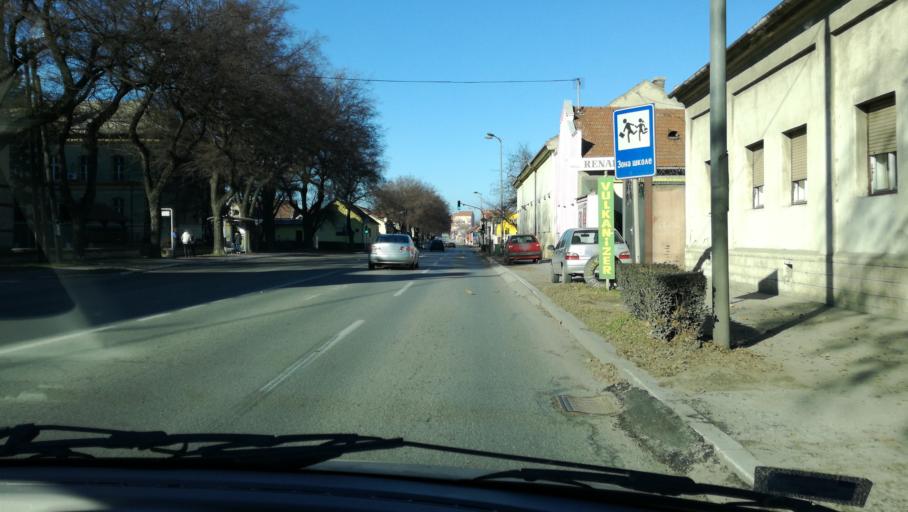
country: RS
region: Autonomna Pokrajina Vojvodina
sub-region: Severnobacki Okrug
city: Subotica
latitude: 46.0892
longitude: 19.6662
